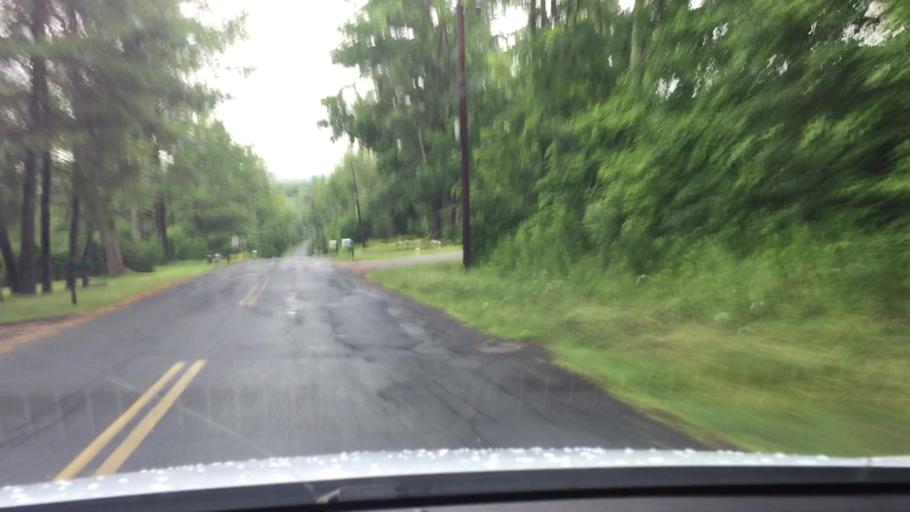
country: US
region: Massachusetts
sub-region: Berkshire County
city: Dalton
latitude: 42.4213
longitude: -73.1918
